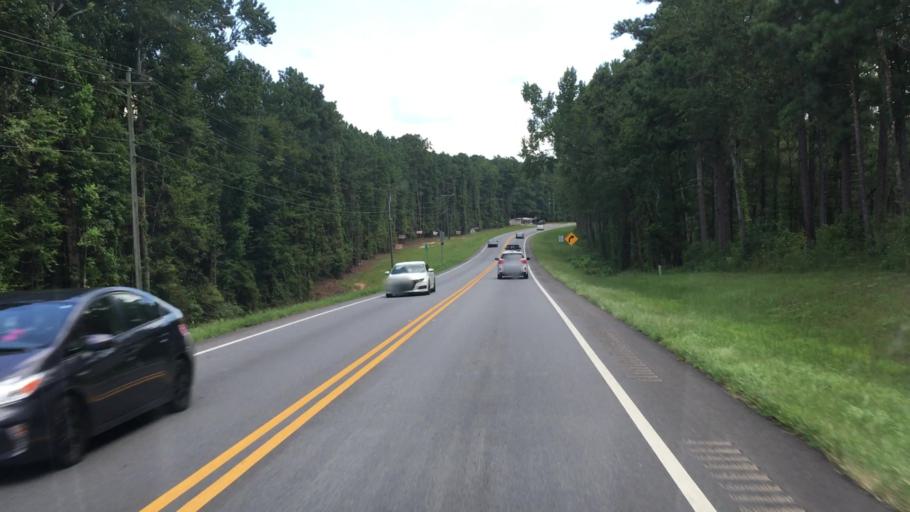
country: US
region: Georgia
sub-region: Putnam County
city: Jefferson
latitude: 33.4087
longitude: -83.3693
